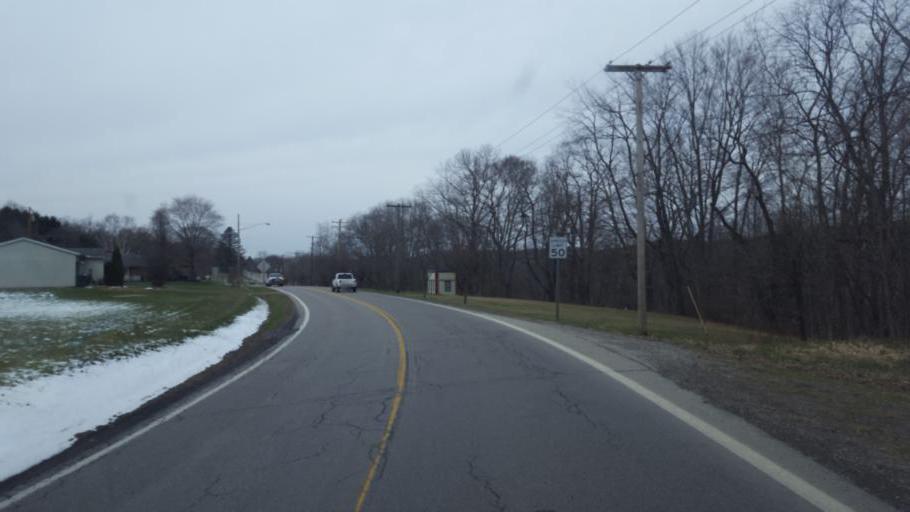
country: US
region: Ohio
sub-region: Sandusky County
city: Bellville
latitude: 40.5945
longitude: -82.4290
